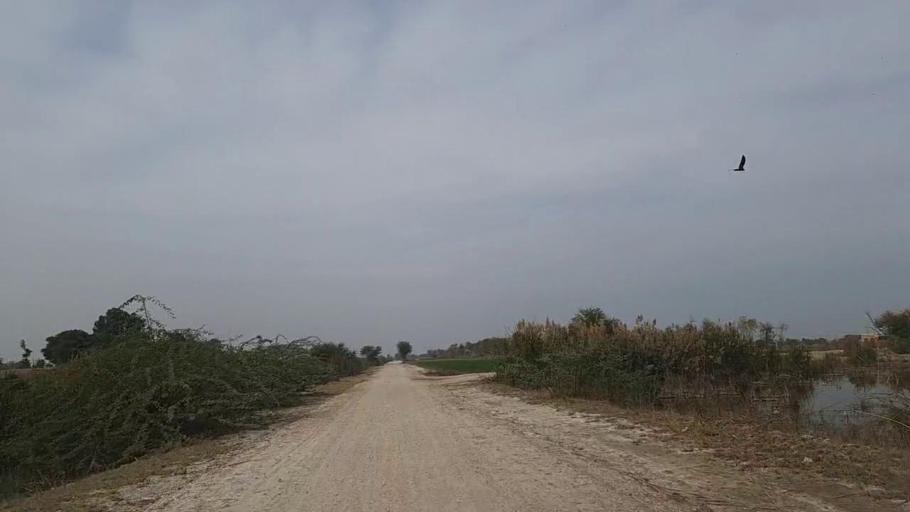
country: PK
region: Sindh
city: Daur
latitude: 26.4147
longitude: 68.4271
